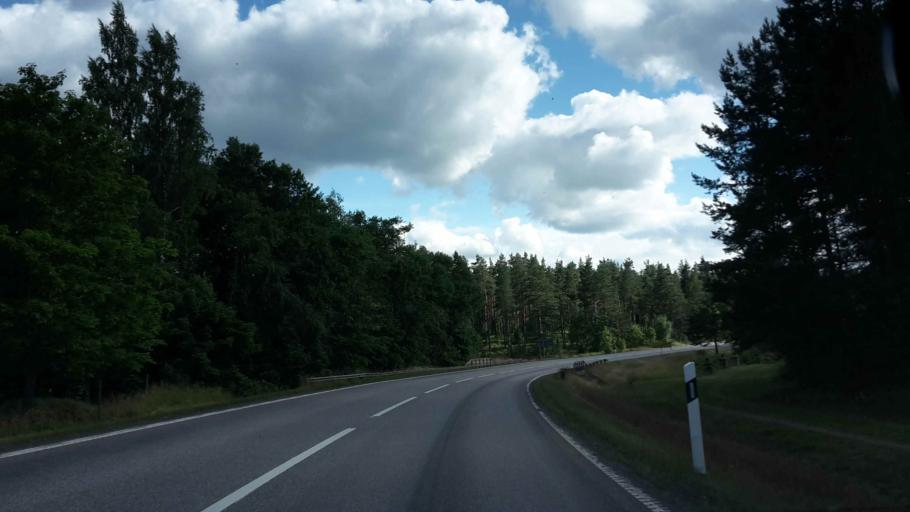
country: SE
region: OErebro
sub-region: Hallsbergs Kommun
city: Palsboda
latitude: 58.8637
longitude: 15.4128
